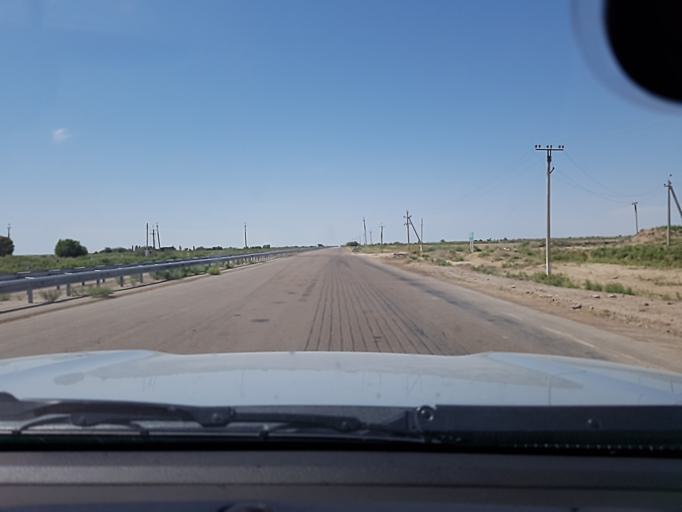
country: TM
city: Akdepe
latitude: 41.7360
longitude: 59.0808
